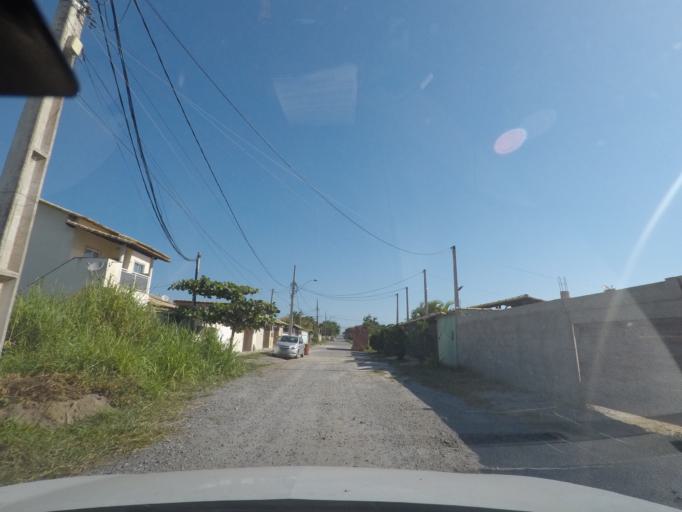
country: BR
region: Rio de Janeiro
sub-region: Marica
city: Marica
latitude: -22.9662
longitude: -42.9190
